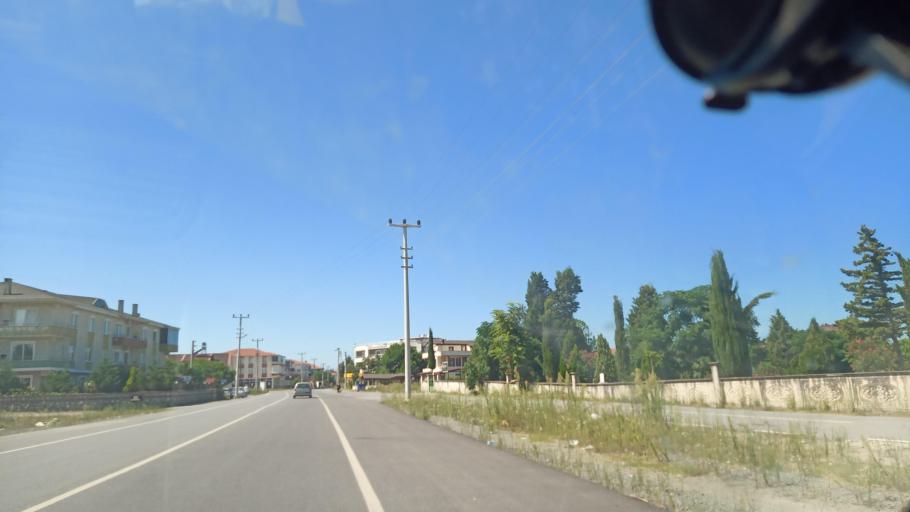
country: TR
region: Sakarya
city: Karasu
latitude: 41.1195
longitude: 30.6561
